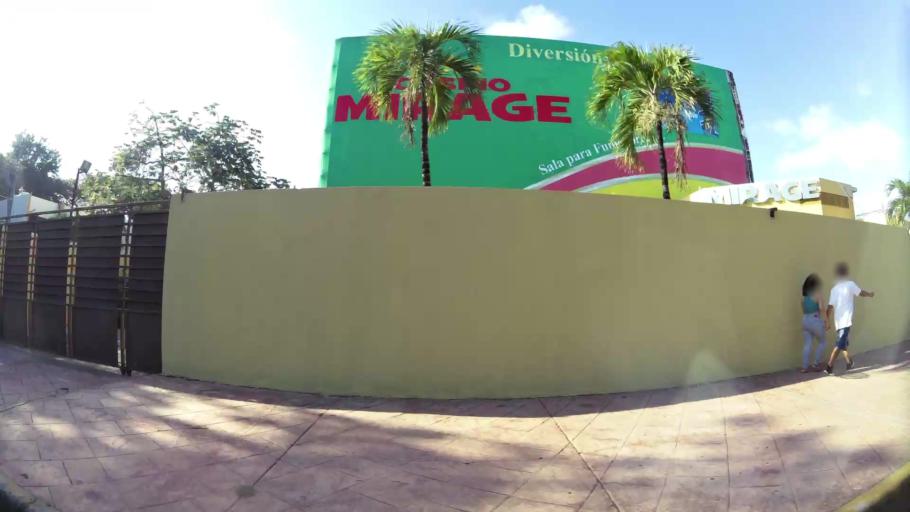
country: DO
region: Nacional
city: Ciudad Nueva
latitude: 18.4568
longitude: -69.9138
